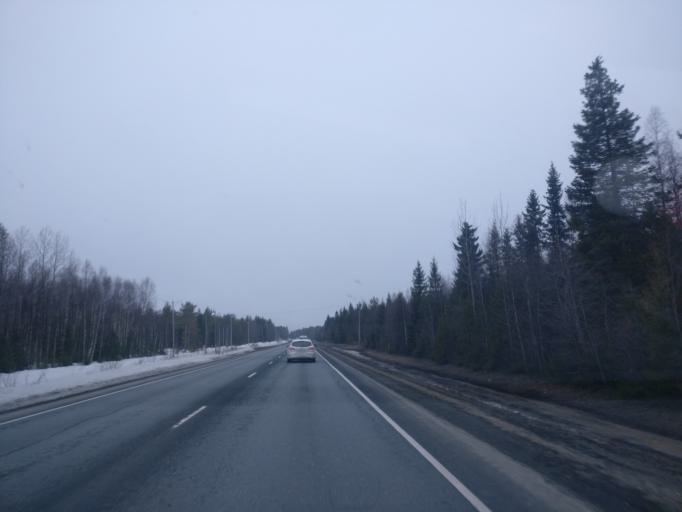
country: FI
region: Lapland
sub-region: Kemi-Tornio
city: Simo
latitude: 65.6716
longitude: 24.9154
